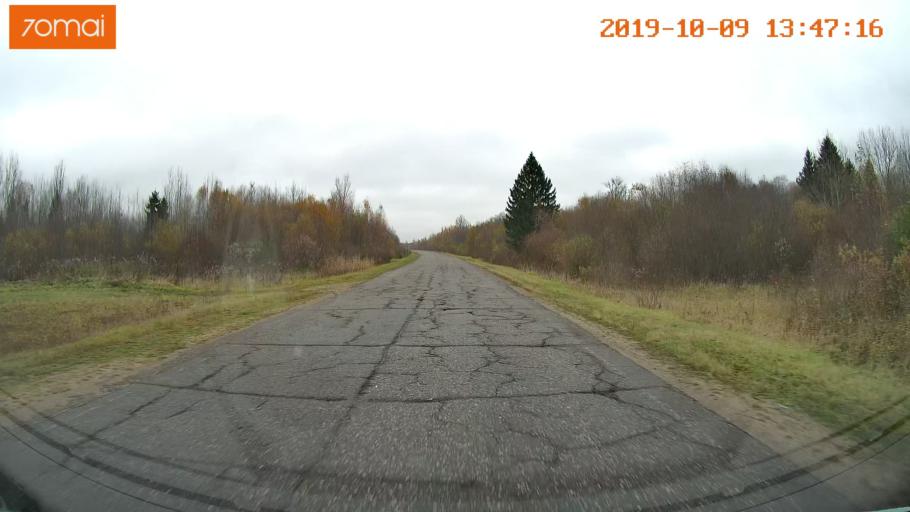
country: RU
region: Kostroma
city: Buy
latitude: 58.3904
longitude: 41.2236
